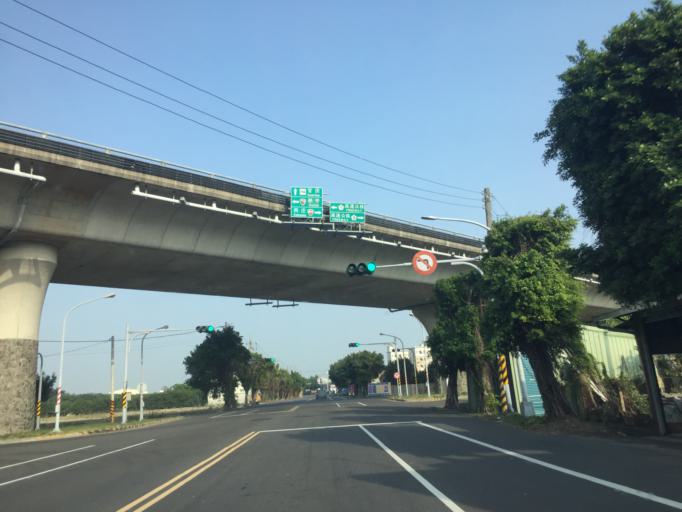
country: TW
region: Taiwan
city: Xinying
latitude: 23.1895
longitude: 120.2750
